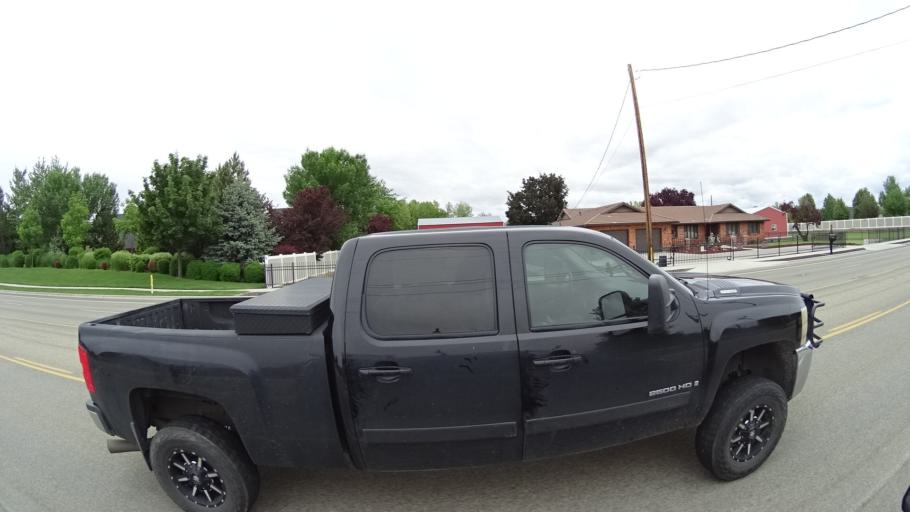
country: US
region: Idaho
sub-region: Ada County
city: Meridian
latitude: 43.6337
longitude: -116.3615
